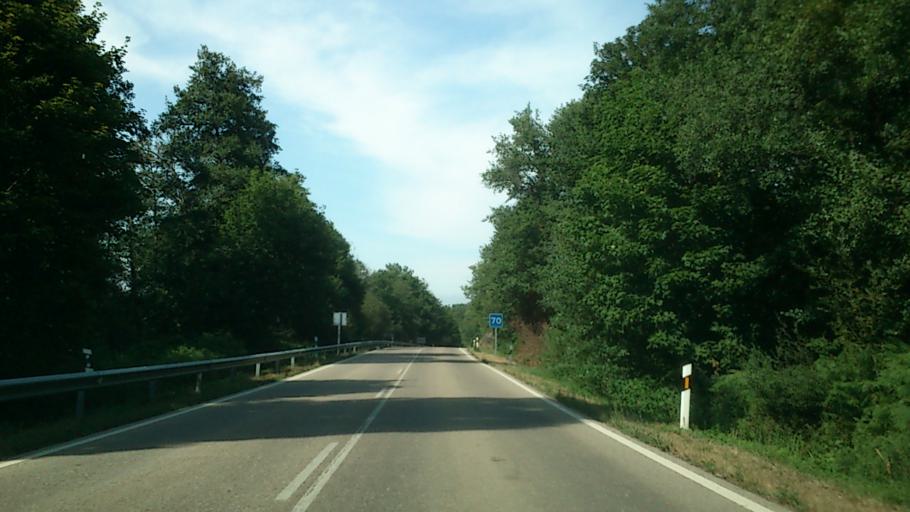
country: ES
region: Castille and Leon
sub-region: Provincia de Burgos
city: Medina de Pomar
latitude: 43.0173
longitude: -3.4835
